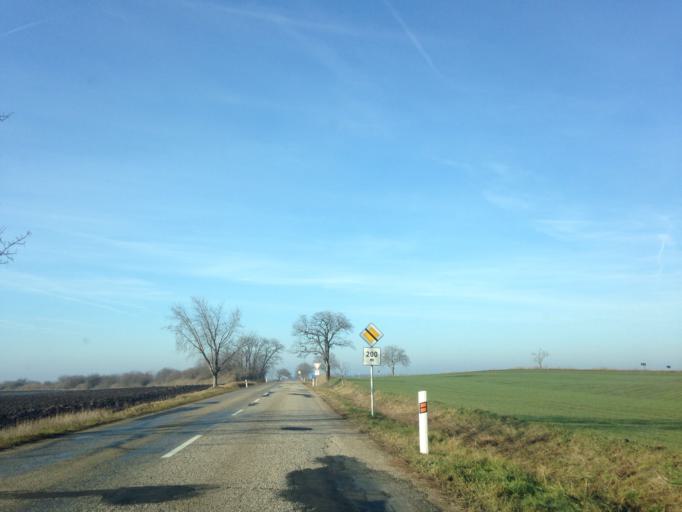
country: SK
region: Nitriansky
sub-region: Okres Nove Zamky
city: Nove Zamky
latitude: 47.9893
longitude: 18.3328
